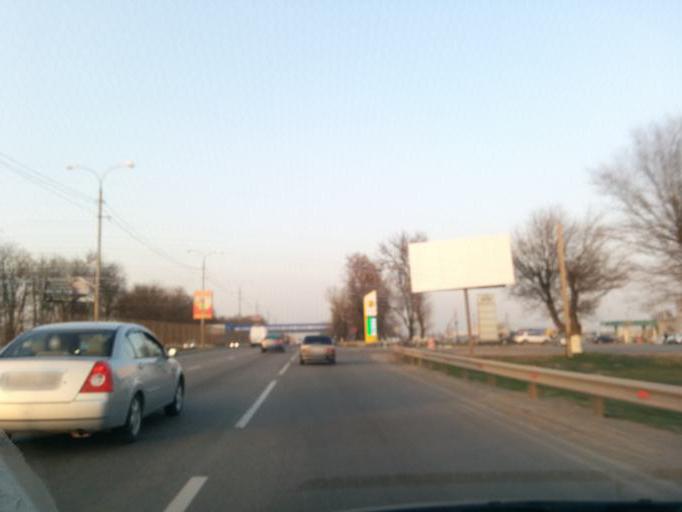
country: RU
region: Rostov
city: Aksay
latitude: 47.2743
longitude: 39.8281
